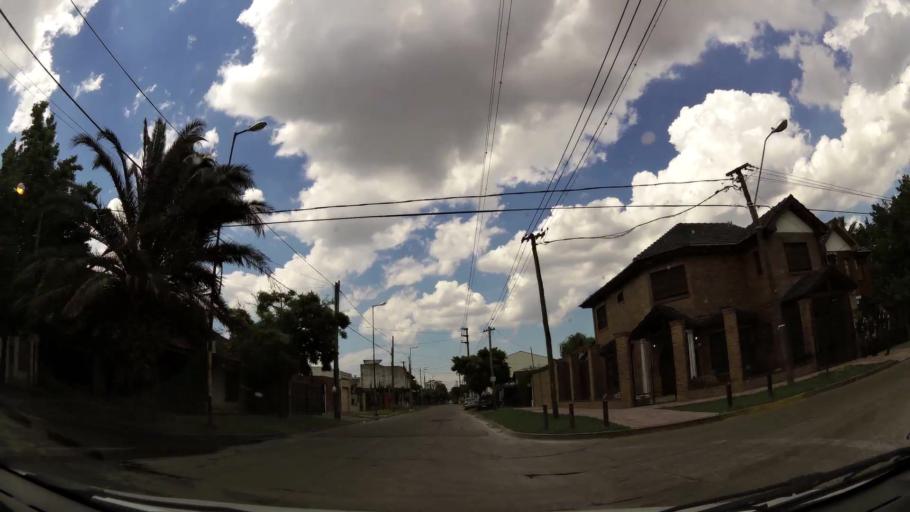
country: AR
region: Buenos Aires
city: Ituzaingo
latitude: -34.6432
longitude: -58.6769
